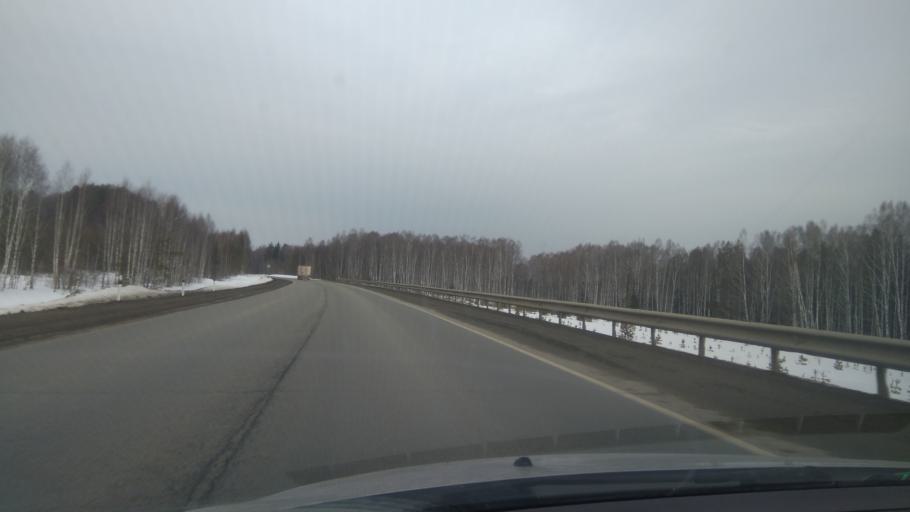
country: RU
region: Sverdlovsk
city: Ufimskiy
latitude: 56.7847
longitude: 58.3932
